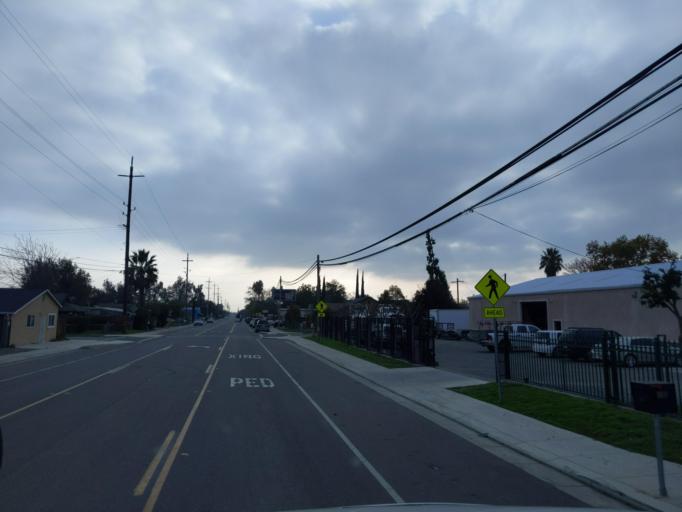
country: US
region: California
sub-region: San Joaquin County
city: August
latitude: 37.9839
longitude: -121.2601
